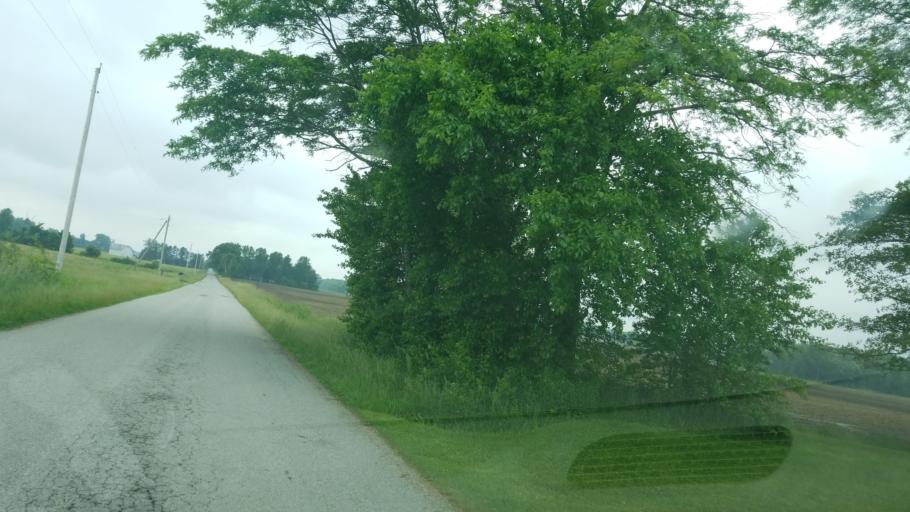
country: US
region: Ohio
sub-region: Morrow County
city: Cardington
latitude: 40.5315
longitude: -82.9484
